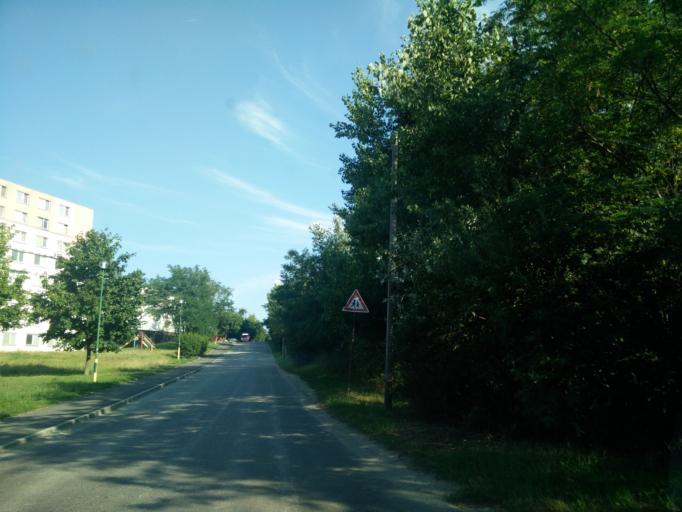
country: AT
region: Lower Austria
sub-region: Politischer Bezirk Bruck an der Leitha
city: Wolfsthal
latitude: 48.1967
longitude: 17.0386
